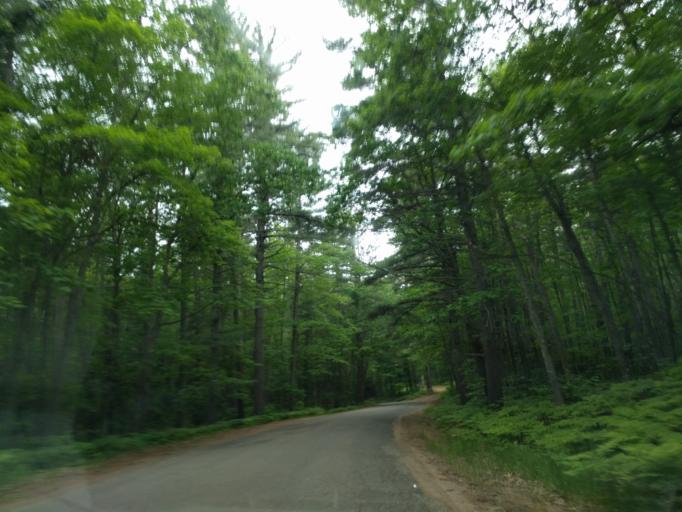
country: US
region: Michigan
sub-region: Marquette County
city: Trowbridge Park
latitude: 46.5753
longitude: -87.4755
